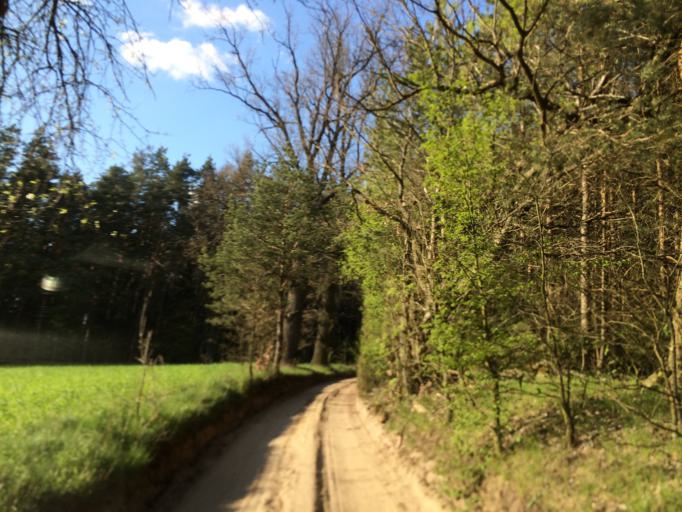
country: PL
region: Warmian-Masurian Voivodeship
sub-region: Powiat dzialdowski
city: Lidzbark
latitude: 53.2301
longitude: 19.7652
